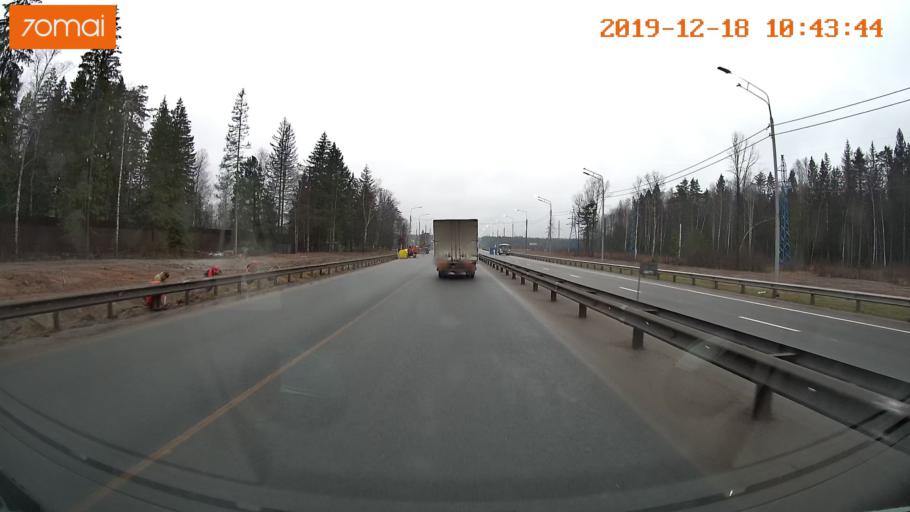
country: RU
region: Moskovskaya
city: Aprelevka
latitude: 55.4692
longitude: 37.0809
